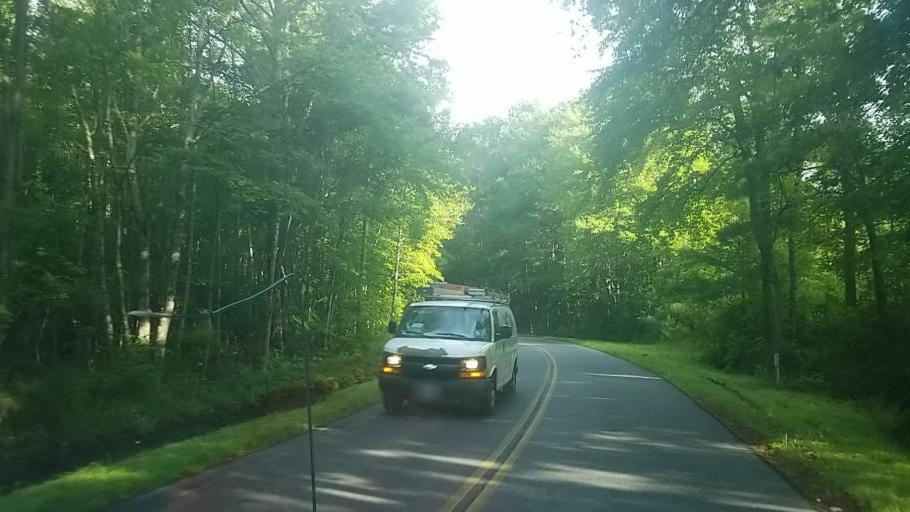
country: US
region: Maryland
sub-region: Worcester County
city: West Ocean City
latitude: 38.3211
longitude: -75.1469
